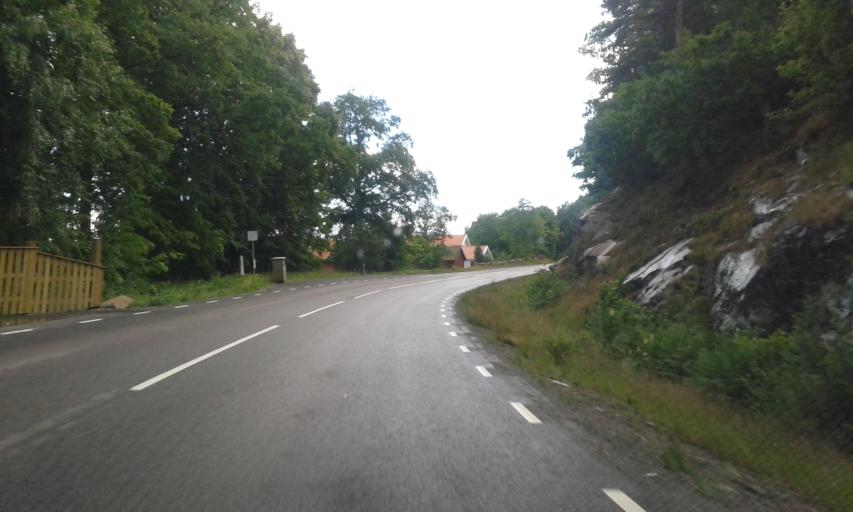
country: SE
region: Vaestra Goetaland
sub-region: Ale Kommun
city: Alvangen
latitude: 57.9642
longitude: 12.1010
